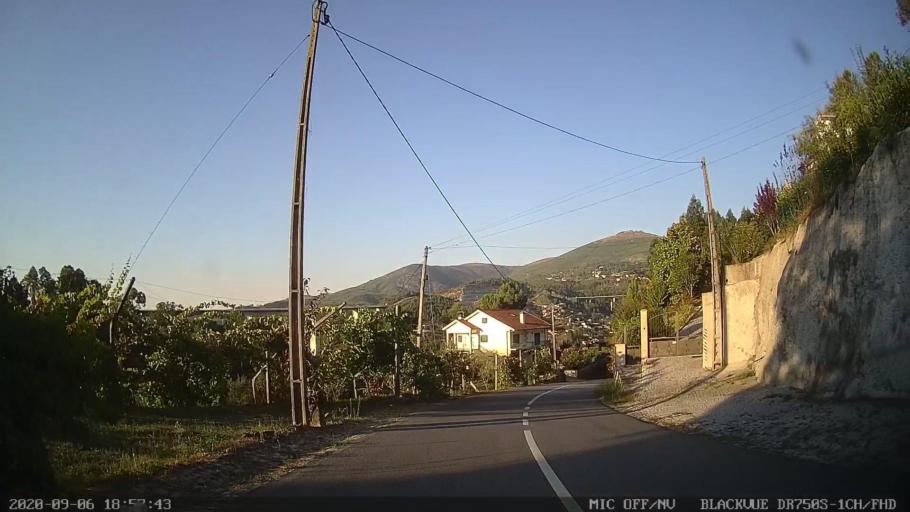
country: PT
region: Porto
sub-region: Baiao
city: Baiao
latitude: 41.2452
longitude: -7.9867
